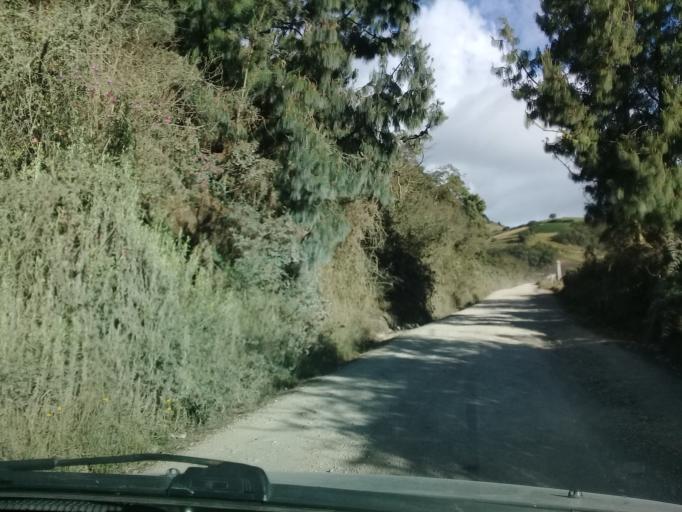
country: CO
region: Cundinamarca
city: Lenguazaque
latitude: 5.2517
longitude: -73.6686
